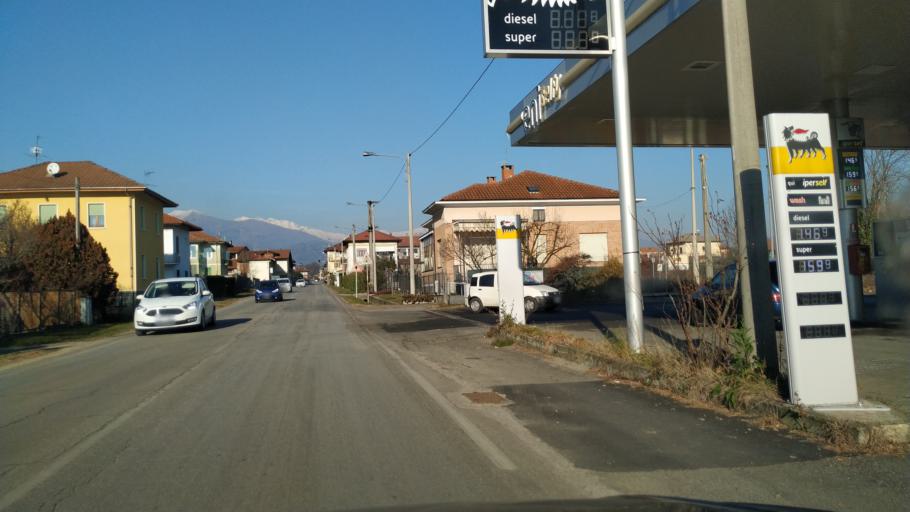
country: IT
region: Piedmont
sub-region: Provincia di Biella
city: Ceresane-Curanuova
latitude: 45.5257
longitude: 8.0104
